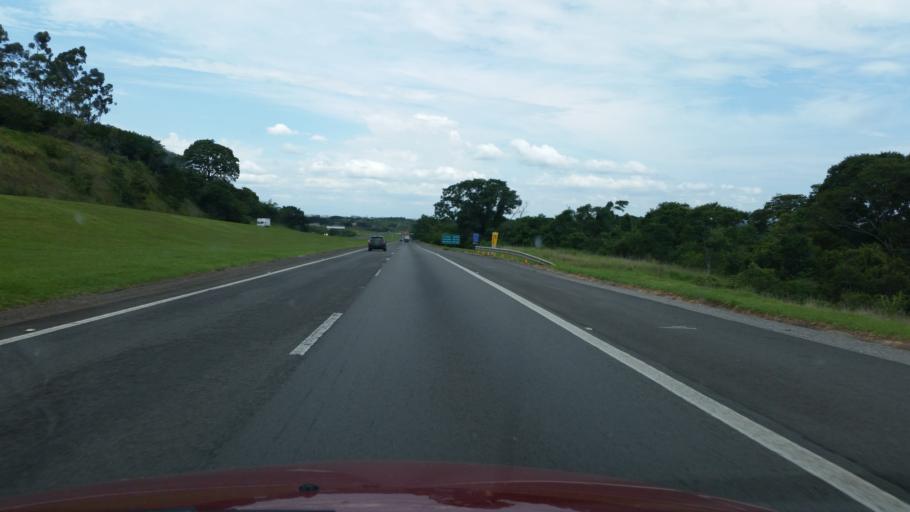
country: BR
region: Sao Paulo
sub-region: Porangaba
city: Porangaba
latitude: -23.2309
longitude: -48.1610
